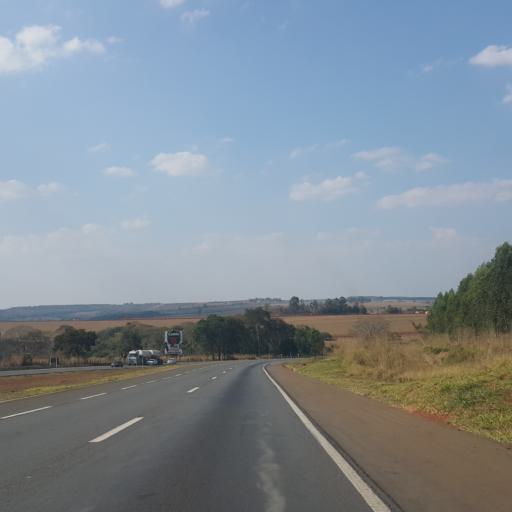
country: BR
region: Goias
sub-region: Abadiania
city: Abadiania
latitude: -16.2798
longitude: -48.7904
